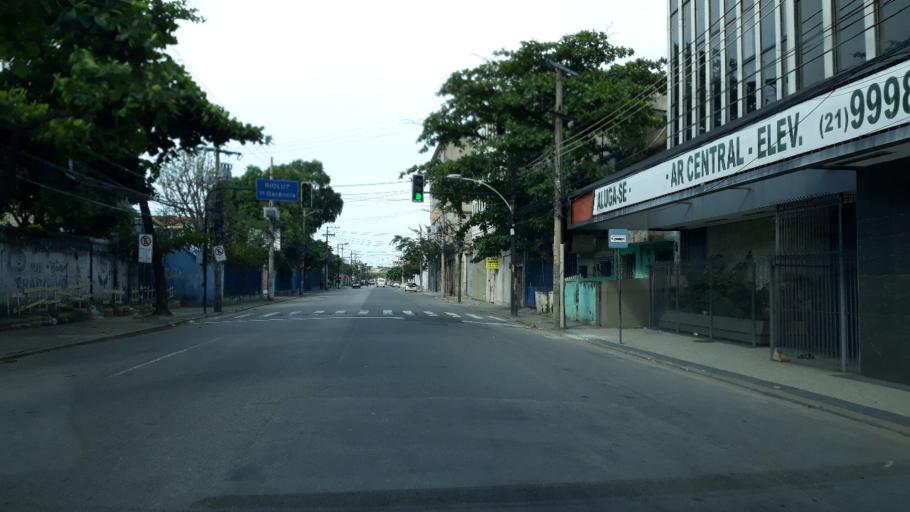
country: BR
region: Rio de Janeiro
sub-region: Rio De Janeiro
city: Rio de Janeiro
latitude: -22.8926
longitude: -43.2371
